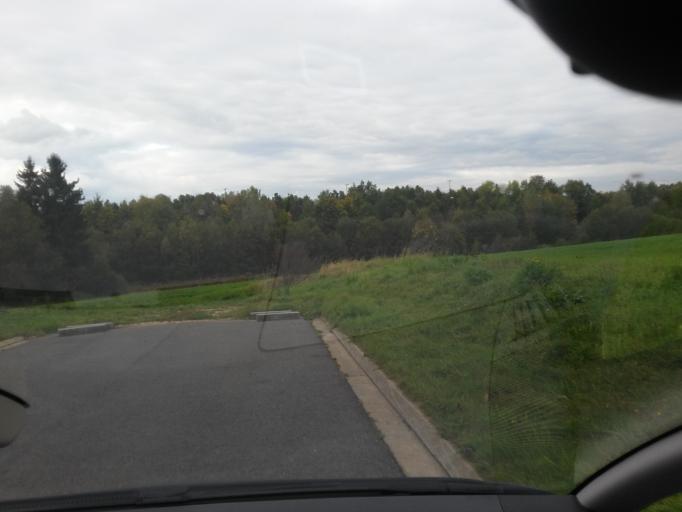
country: BE
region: Wallonia
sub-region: Province du Luxembourg
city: Arlon
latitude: 49.6950
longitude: 5.8072
